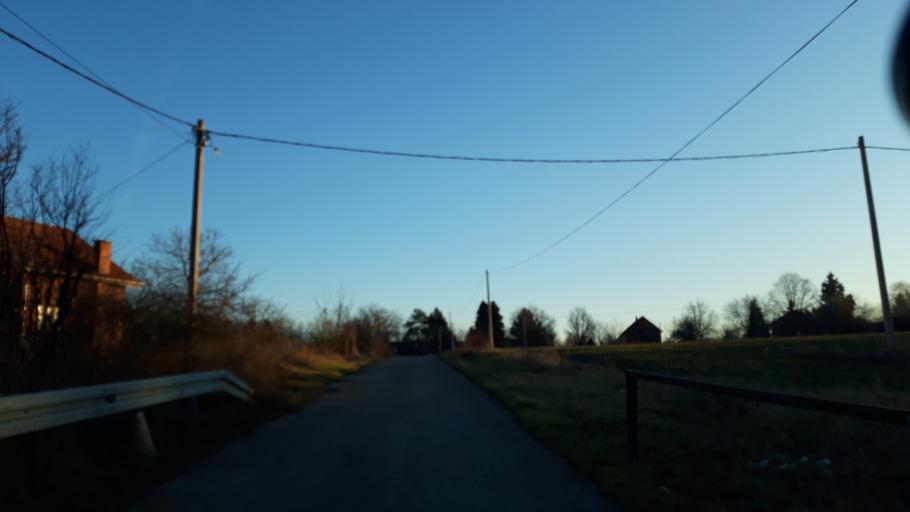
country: RS
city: Cortanovci
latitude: 45.1604
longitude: 20.0026
